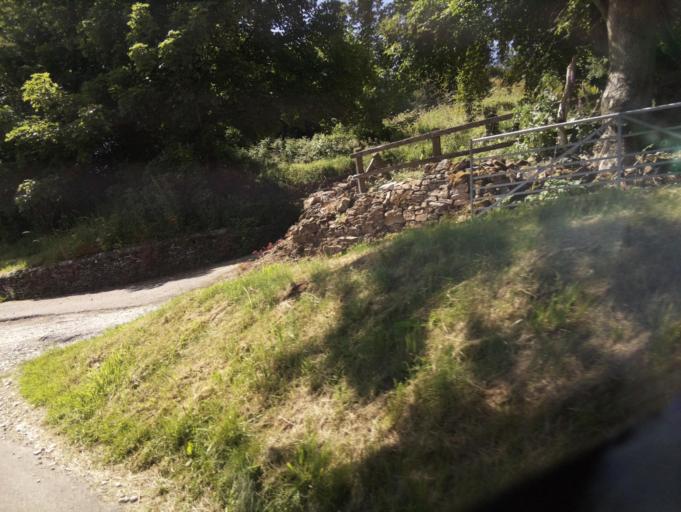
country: GB
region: England
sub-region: Derbyshire
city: Buxton
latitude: 53.1927
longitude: -1.8790
